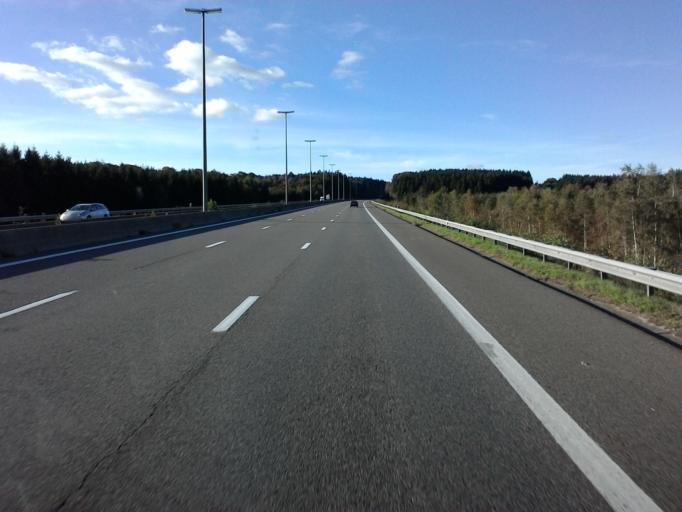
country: BE
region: Wallonia
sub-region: Province du Luxembourg
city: Houffalize
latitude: 50.1785
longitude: 5.7860
